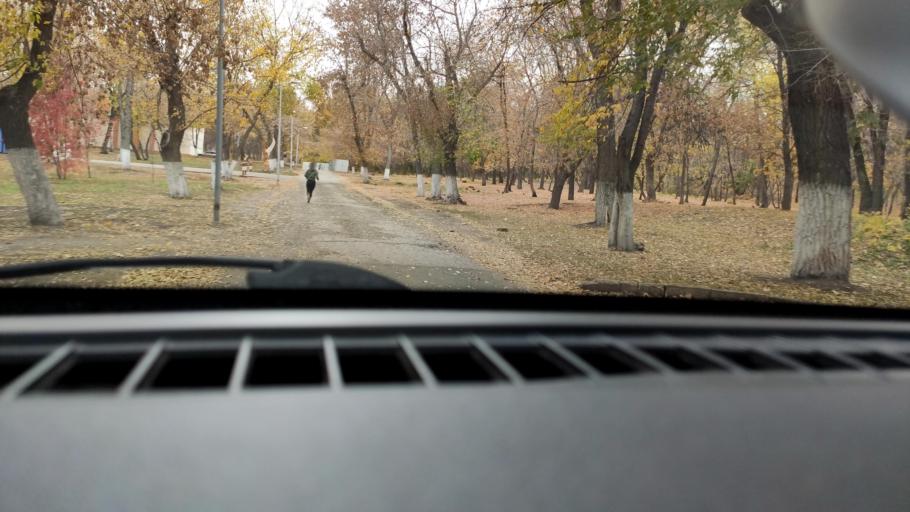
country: RU
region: Samara
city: Samara
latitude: 53.2039
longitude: 50.2210
